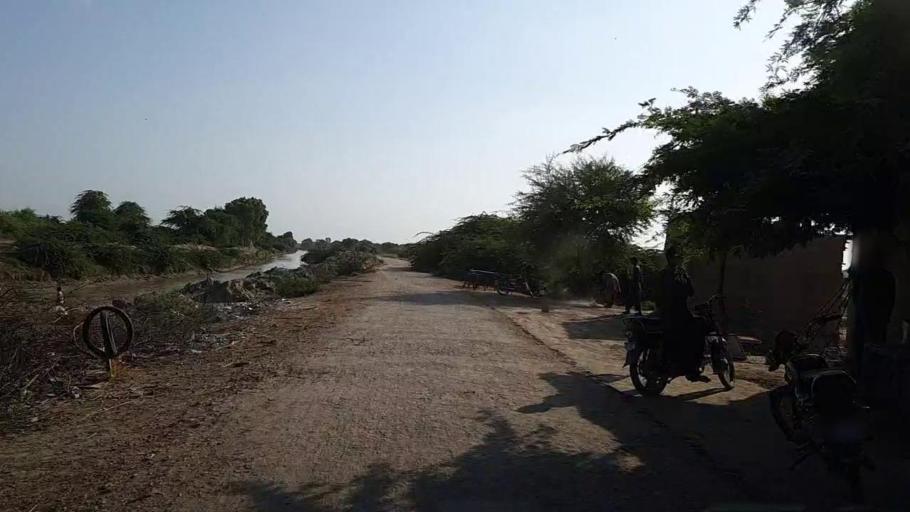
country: PK
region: Sindh
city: Kario
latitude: 24.7968
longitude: 68.6739
